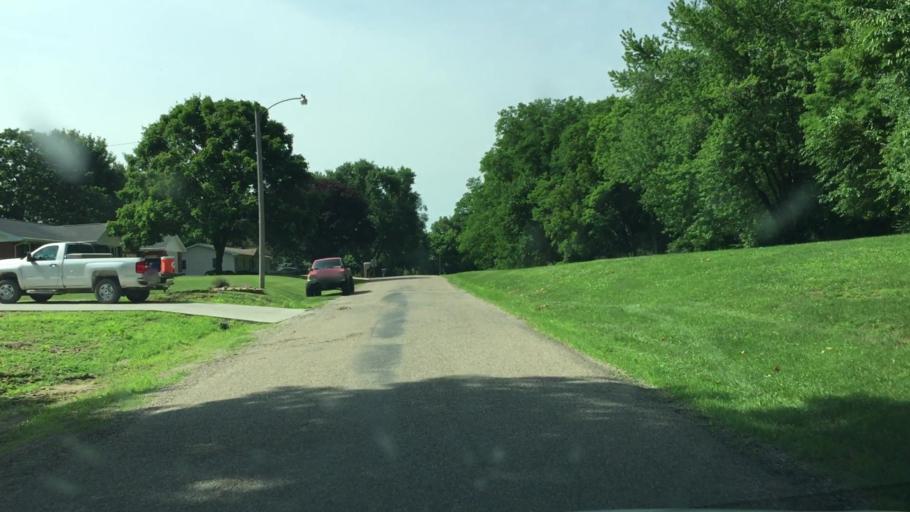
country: US
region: Illinois
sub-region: Hancock County
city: Nauvoo
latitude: 40.5451
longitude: -91.3754
